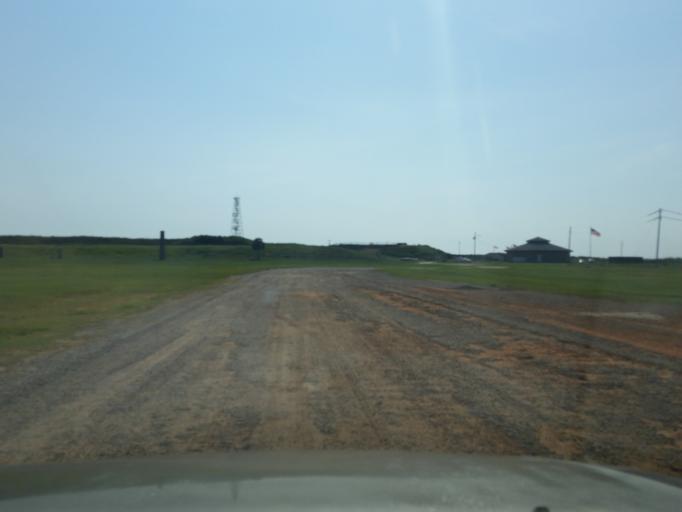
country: US
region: Alabama
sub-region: Mobile County
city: Dauphin Island
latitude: 30.2292
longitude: -88.0197
